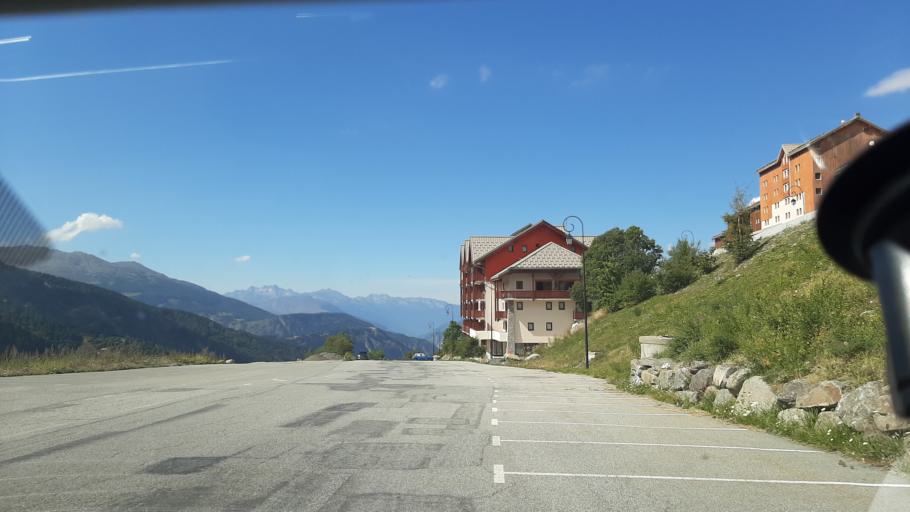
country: FR
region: Rhone-Alpes
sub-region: Departement de la Savoie
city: Saint-Michel-de-Maurienne
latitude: 45.1711
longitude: 6.4951
